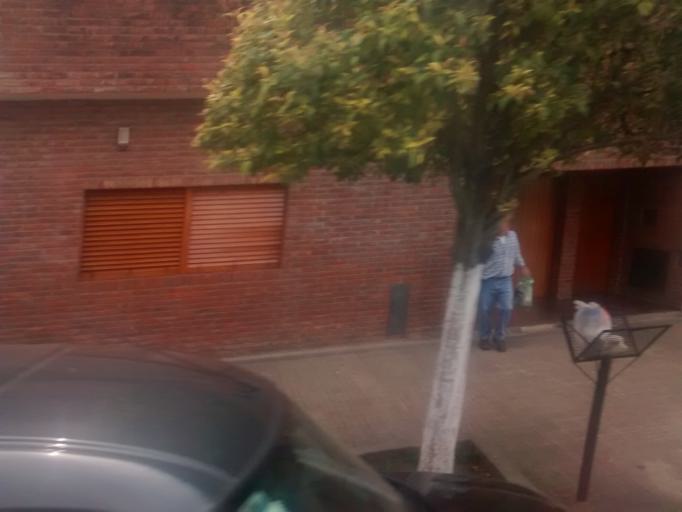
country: AR
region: Buenos Aires
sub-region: Partido de La Plata
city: La Plata
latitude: -34.9271
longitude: -57.9298
